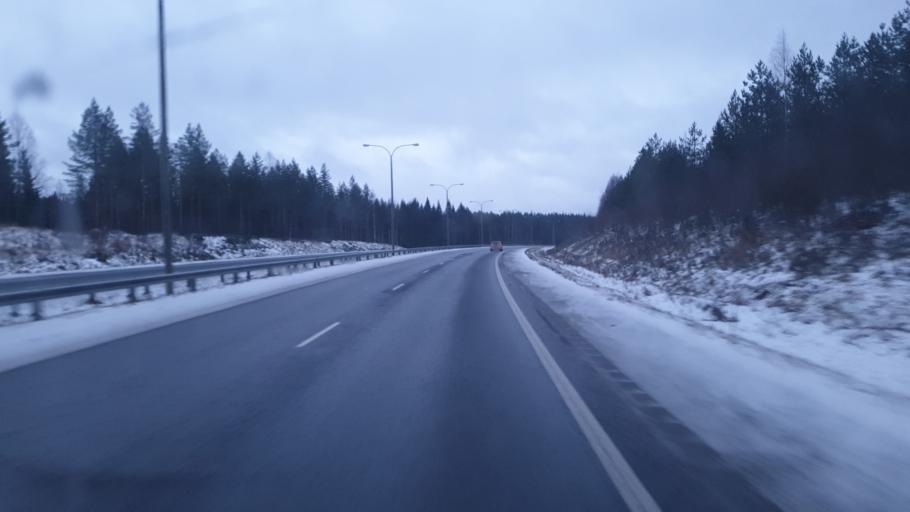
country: FI
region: Northern Savo
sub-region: Kuopio
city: Siilinjaervi
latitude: 63.0127
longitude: 27.6750
